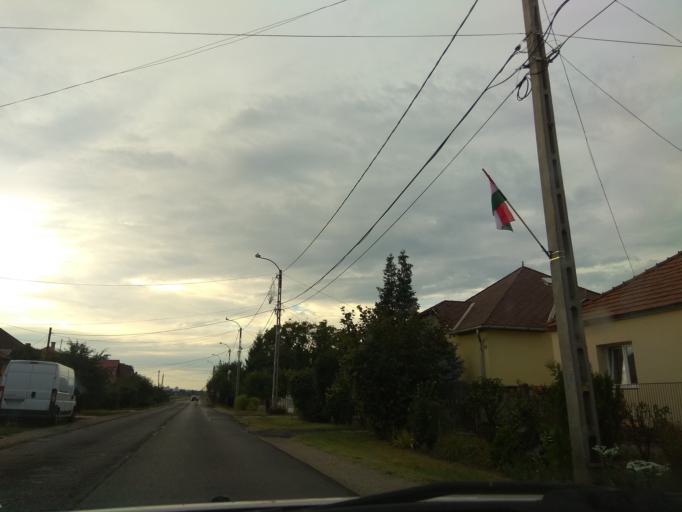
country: HU
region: Borsod-Abauj-Zemplen
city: Miskolc
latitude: 48.0763
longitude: 20.8248
